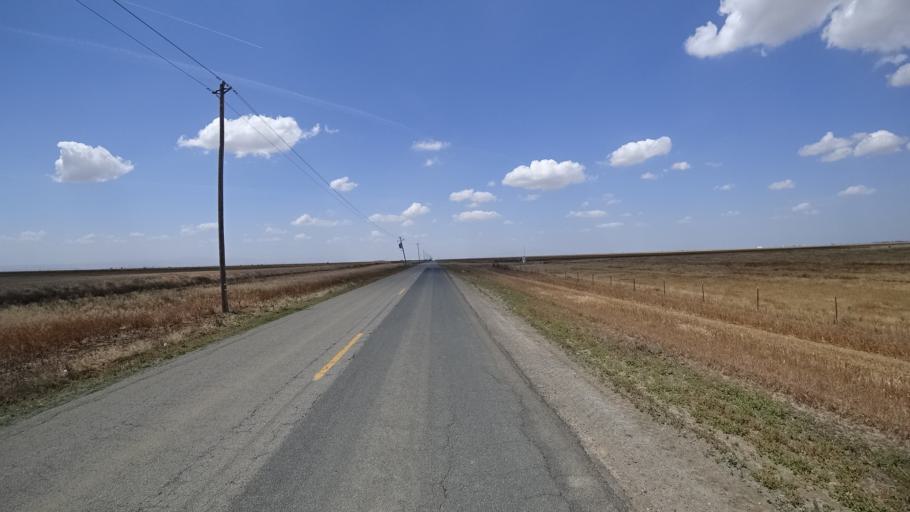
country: US
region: California
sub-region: Kings County
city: Stratford
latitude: 36.1894
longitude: -119.8853
